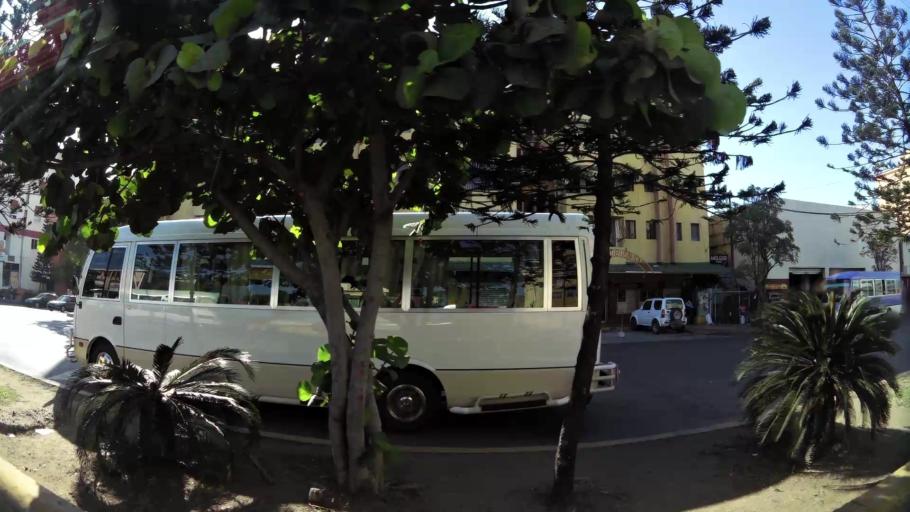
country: DO
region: Nacional
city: San Carlos
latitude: 18.4798
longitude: -69.8881
